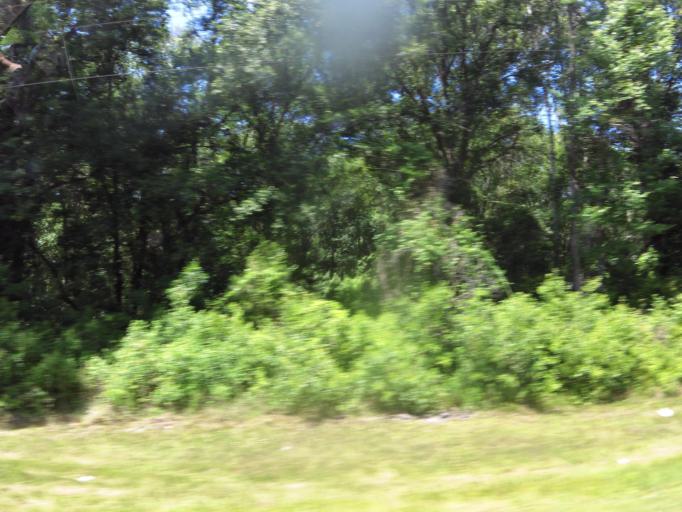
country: US
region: Florida
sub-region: Bradford County
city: Starke
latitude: 30.0287
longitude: -82.0739
